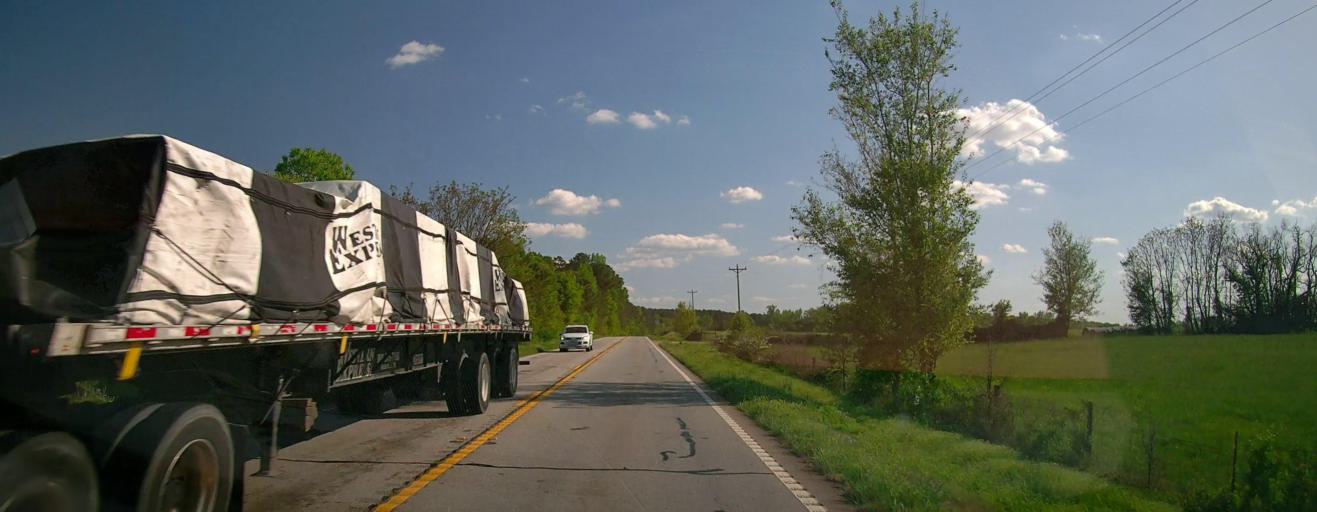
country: US
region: Georgia
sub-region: Morgan County
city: Madison
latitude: 33.5568
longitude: -83.5004
